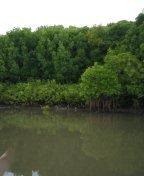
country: IN
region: Kerala
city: Chavakkad
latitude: 10.5380
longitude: 76.0494
